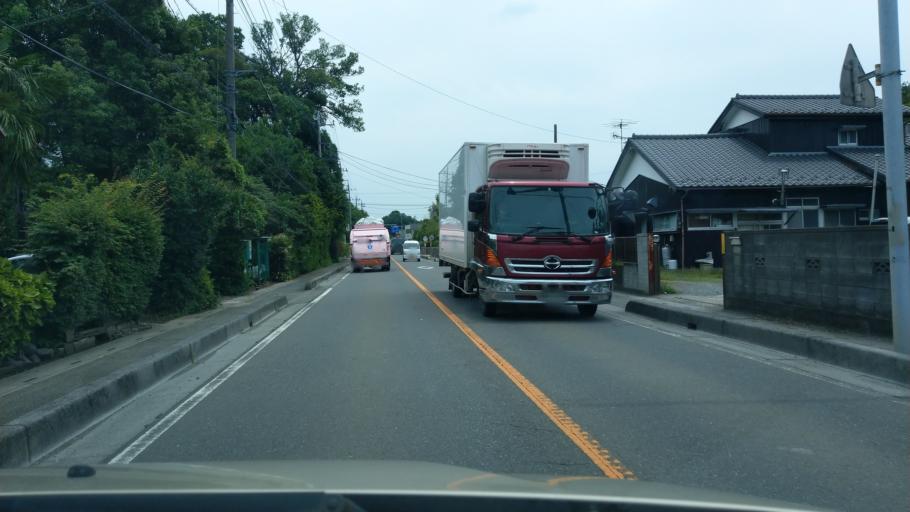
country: JP
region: Saitama
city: Saitama
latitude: 35.9114
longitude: 139.6945
